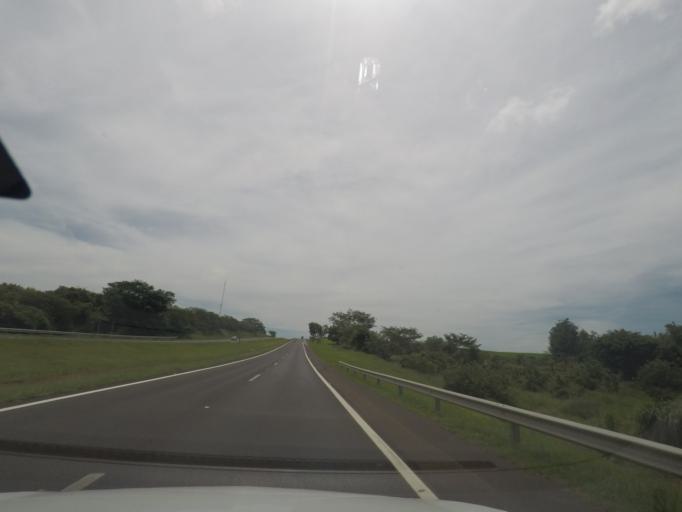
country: BR
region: Sao Paulo
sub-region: Bebedouro
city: Bebedouro
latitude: -20.9713
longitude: -48.4399
